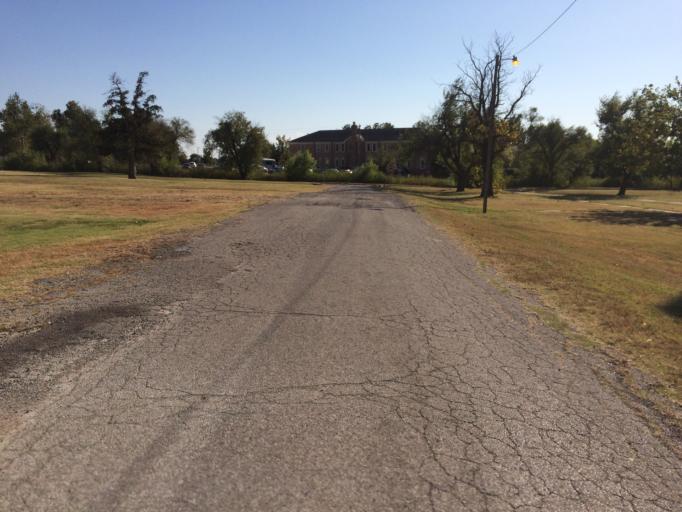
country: US
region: Oklahoma
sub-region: Cleveland County
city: Norman
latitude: 35.2288
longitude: -97.4243
